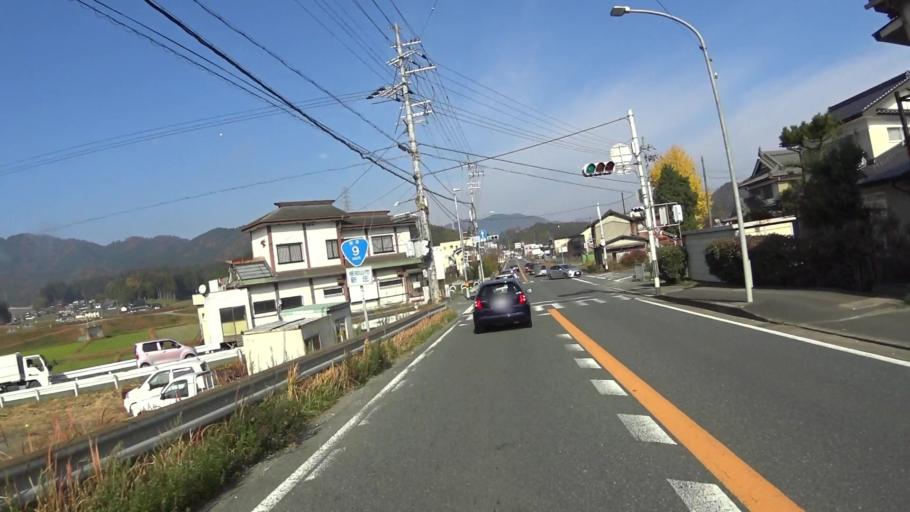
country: JP
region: Kyoto
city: Fukuchiyama
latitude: 35.3061
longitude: 135.1035
